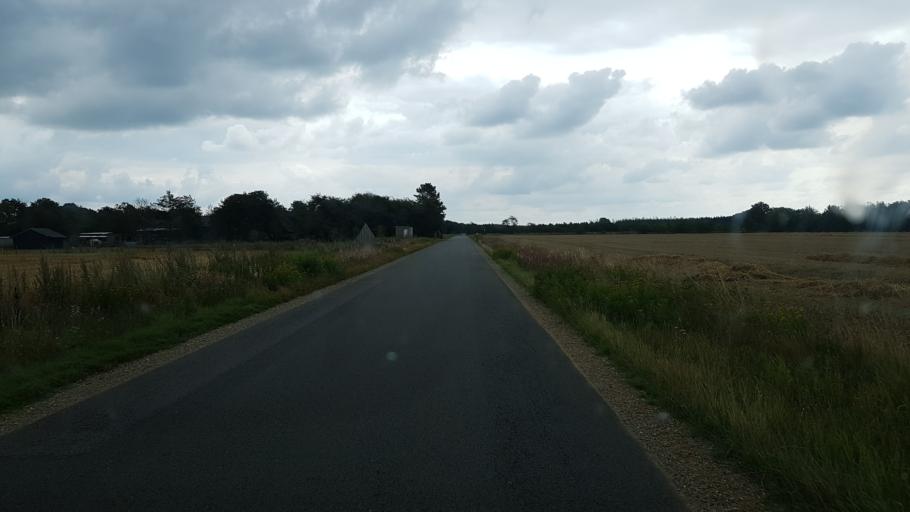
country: DK
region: South Denmark
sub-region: Vejen Kommune
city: Holsted
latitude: 55.6278
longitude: 8.8643
